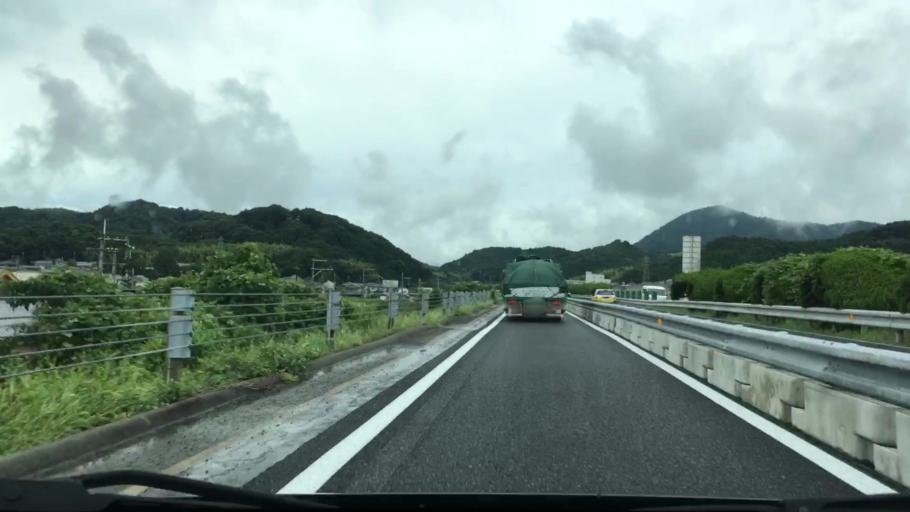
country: JP
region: Hyogo
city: Himeji
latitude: 34.9520
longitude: 134.7478
